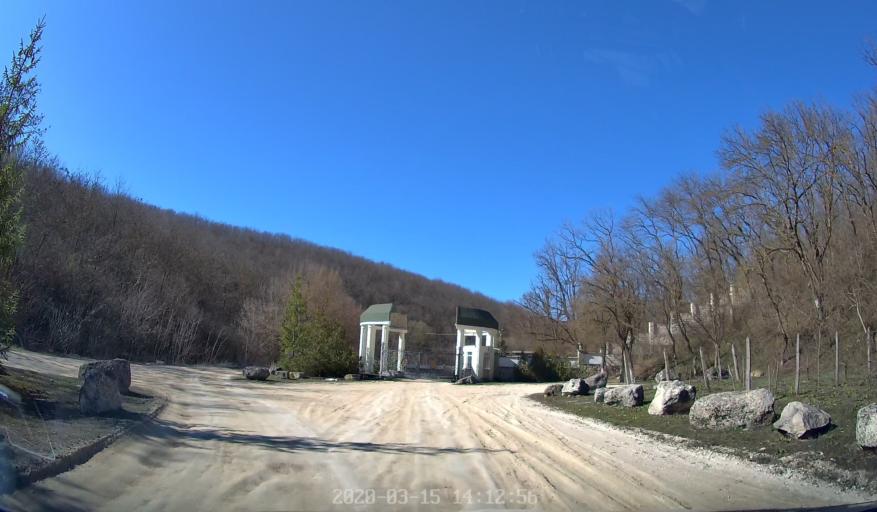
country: MD
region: Orhei
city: Orhei
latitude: 47.3149
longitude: 28.9374
